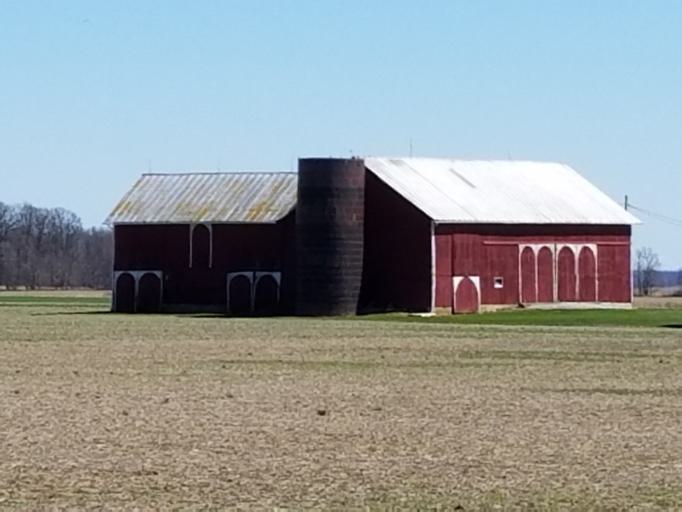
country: US
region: Ohio
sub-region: Crawford County
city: Bucyrus
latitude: 40.9322
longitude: -82.9014
